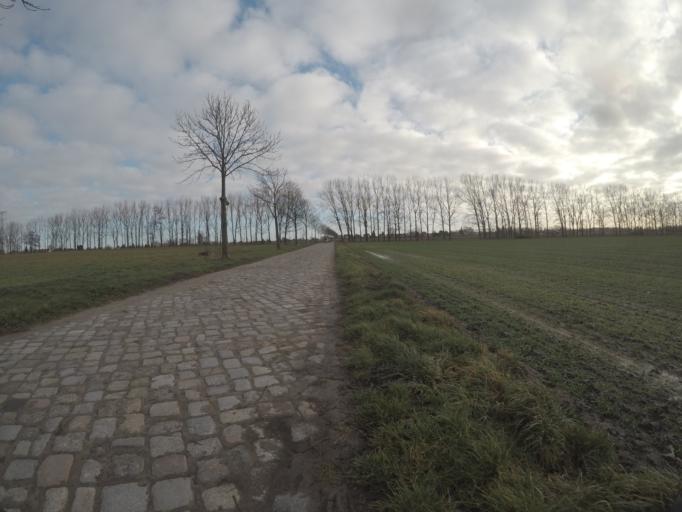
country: DE
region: Berlin
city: Wartenberg
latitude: 52.5899
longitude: 13.5244
